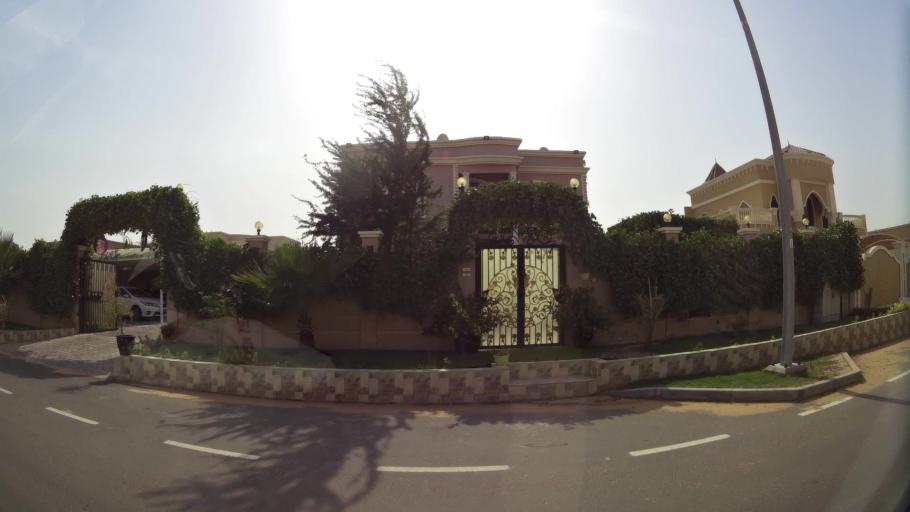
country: AE
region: Ash Shariqah
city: Sharjah
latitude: 25.2585
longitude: 55.4623
